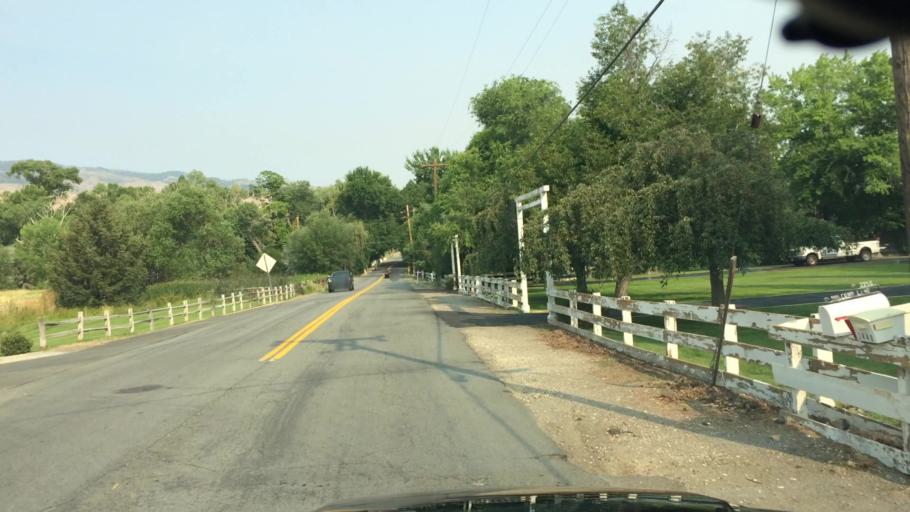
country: US
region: Nevada
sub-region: Washoe County
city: Reno
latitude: 39.4406
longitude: -119.7936
